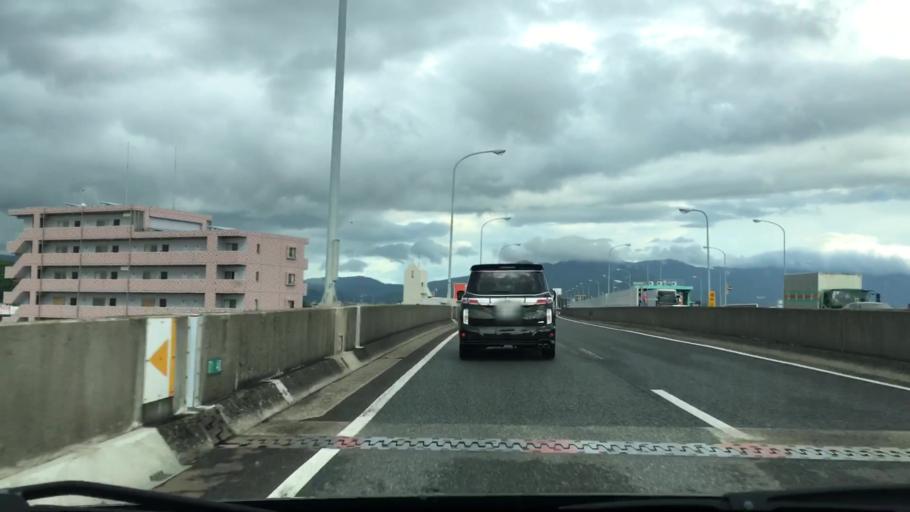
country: JP
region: Fukuoka
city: Fukuoka-shi
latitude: 33.6321
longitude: 130.4336
